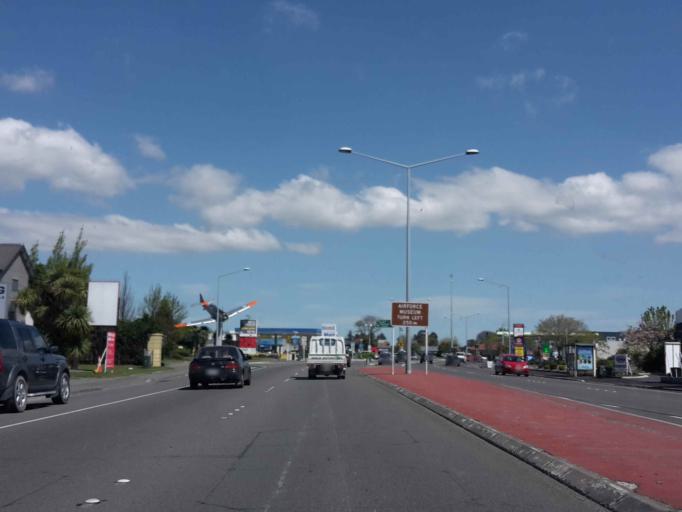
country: NZ
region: Canterbury
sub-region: Selwyn District
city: Prebbleton
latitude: -43.5424
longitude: 172.5479
